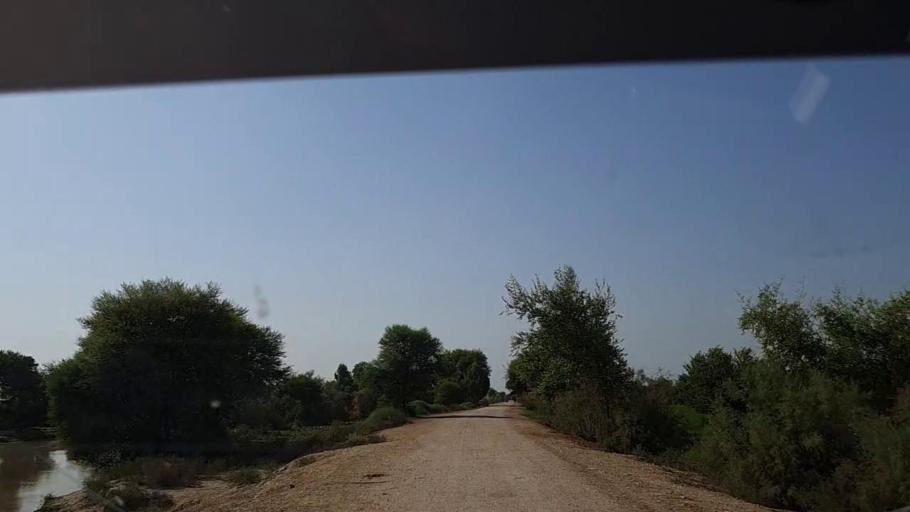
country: PK
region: Sindh
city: Ghauspur
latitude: 28.1905
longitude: 69.0576
